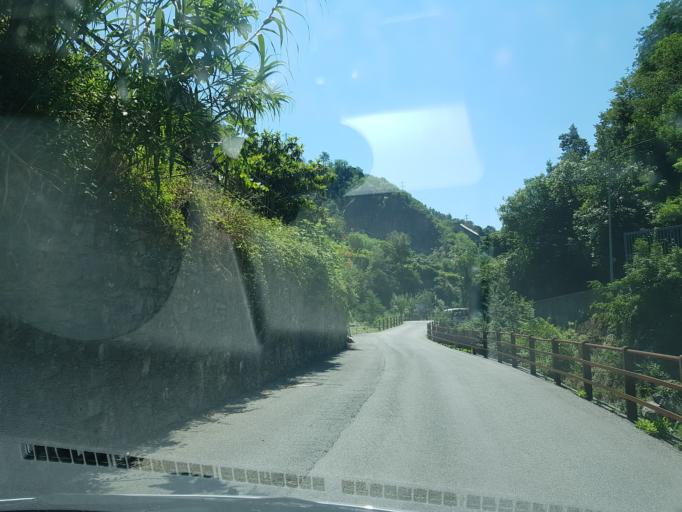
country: IT
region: Liguria
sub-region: Provincia di Genova
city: San Teodoro
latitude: 44.4455
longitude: 8.8542
